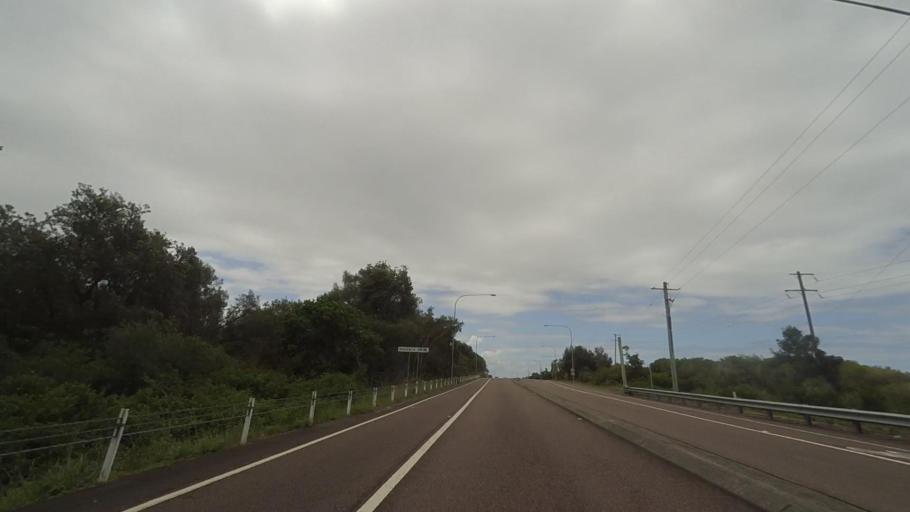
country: AU
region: New South Wales
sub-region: Wyong Shire
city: The Entrance
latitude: -33.3119
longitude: 151.5198
